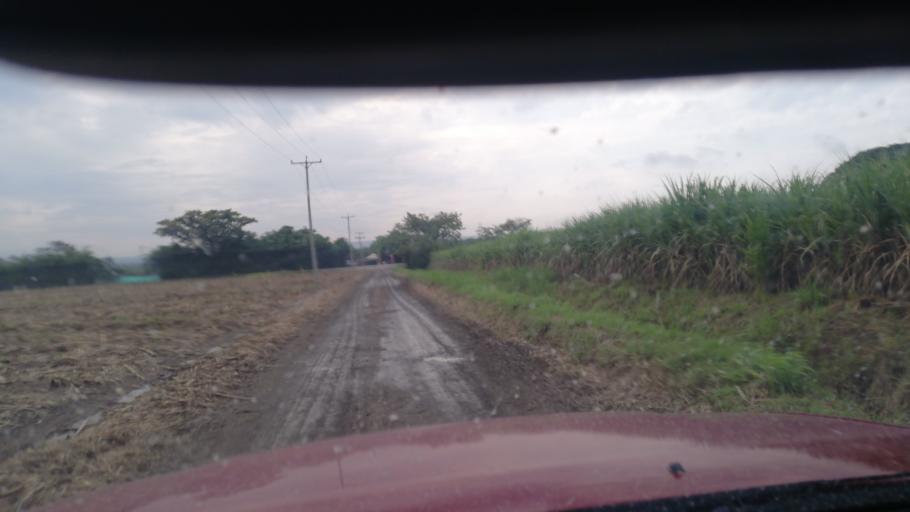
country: CO
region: Risaralda
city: La Virginia
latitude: 4.8732
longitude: -75.9214
